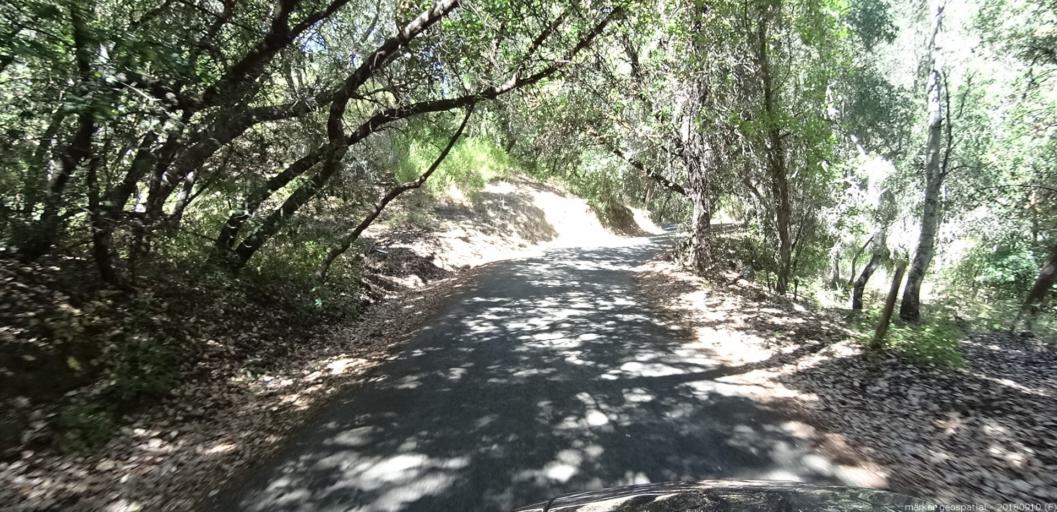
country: US
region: California
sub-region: Monterey County
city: Carmel Valley Village
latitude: 36.4222
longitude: -121.7830
